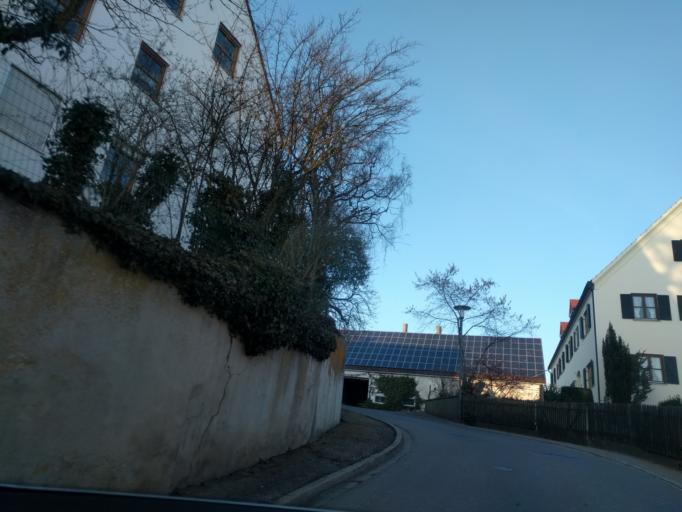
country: DE
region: Bavaria
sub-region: Swabia
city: Donauwoerth
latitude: 48.7128
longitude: 10.7507
